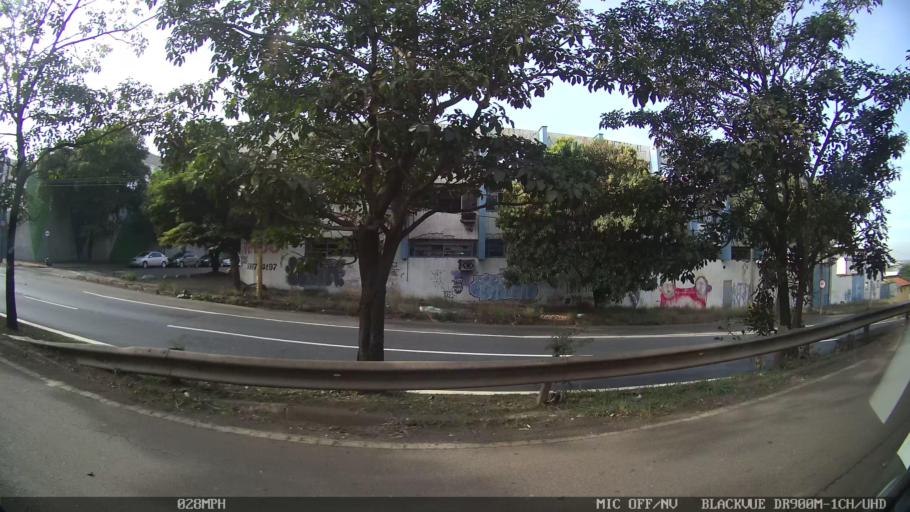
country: BR
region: Sao Paulo
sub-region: Piracicaba
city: Piracicaba
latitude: -22.7009
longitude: -47.6563
